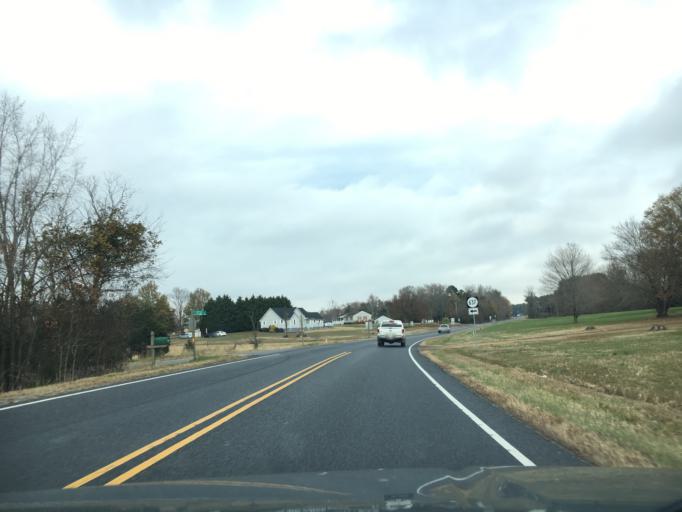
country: US
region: Virginia
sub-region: Prince Edward County
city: Farmville
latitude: 37.3406
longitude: -78.3894
